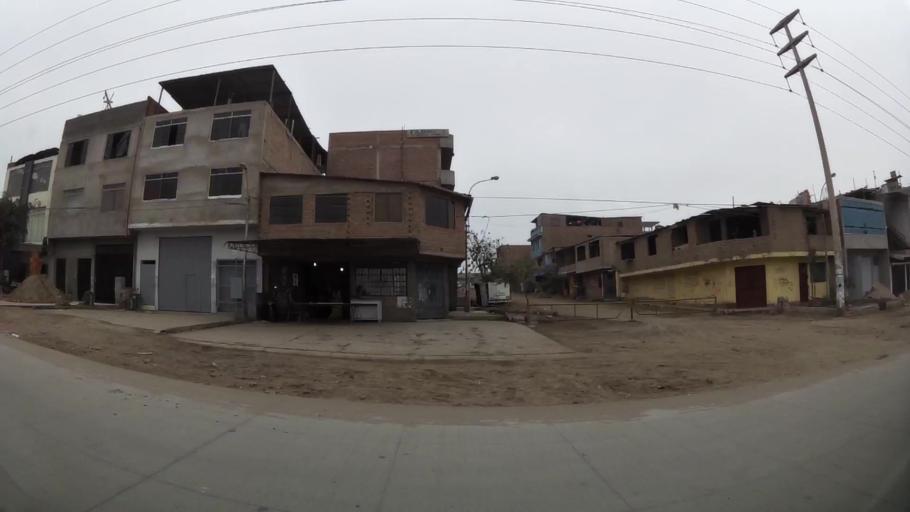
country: PE
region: Lima
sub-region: Lima
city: Surco
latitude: -12.1987
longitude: -76.9405
